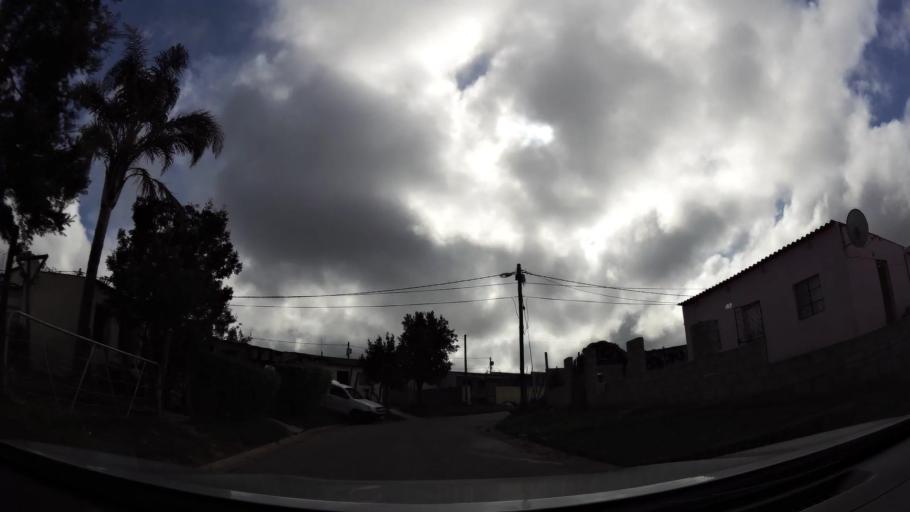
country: ZA
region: Western Cape
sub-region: Eden District Municipality
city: Plettenberg Bay
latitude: -34.0504
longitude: 23.3236
